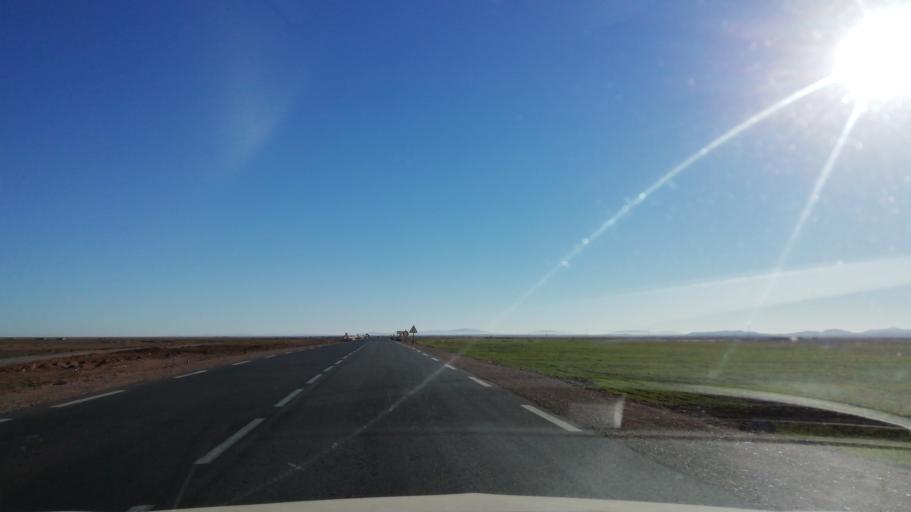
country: DZ
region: El Bayadh
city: El Bayadh
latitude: 33.8594
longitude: 0.5631
